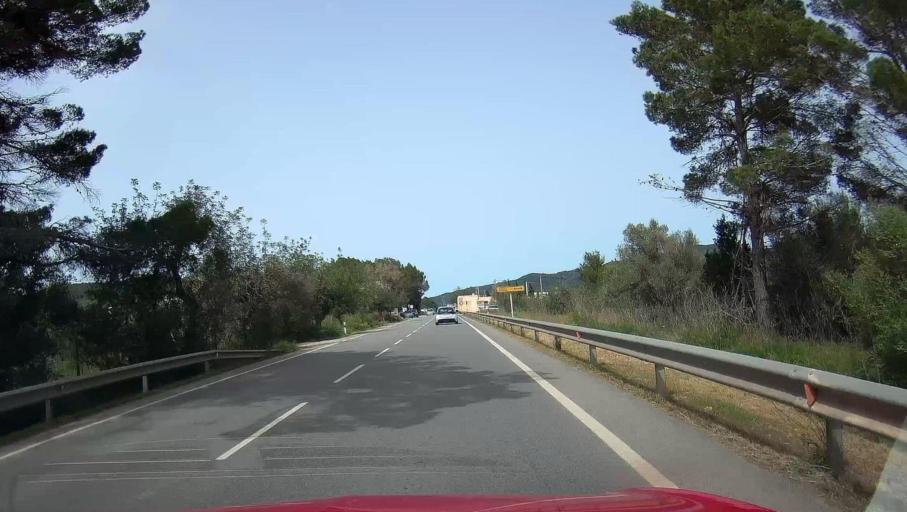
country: ES
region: Balearic Islands
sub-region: Illes Balears
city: Sant Joan de Labritja
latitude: 39.0295
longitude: 1.4887
